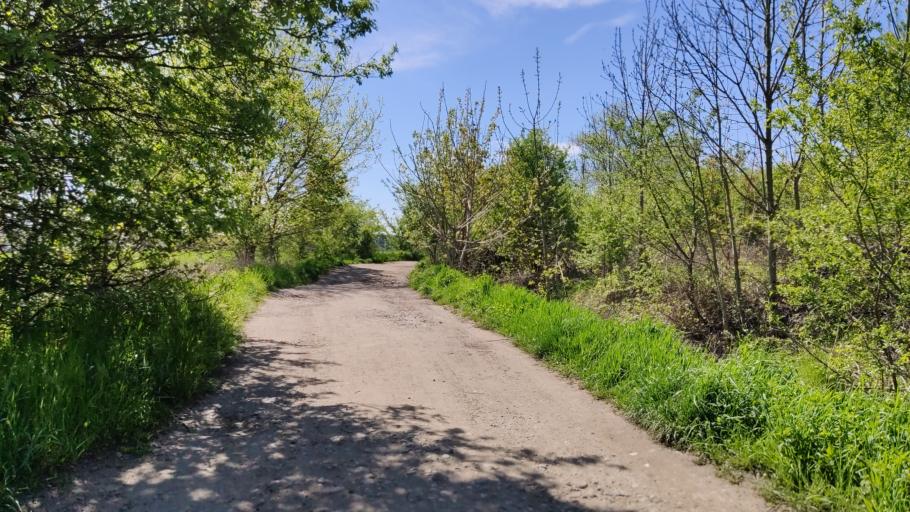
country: PL
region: Lower Silesian Voivodeship
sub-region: Powiat wroclawski
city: Zerniki Wroclawskie
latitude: 51.0599
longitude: 17.0450
